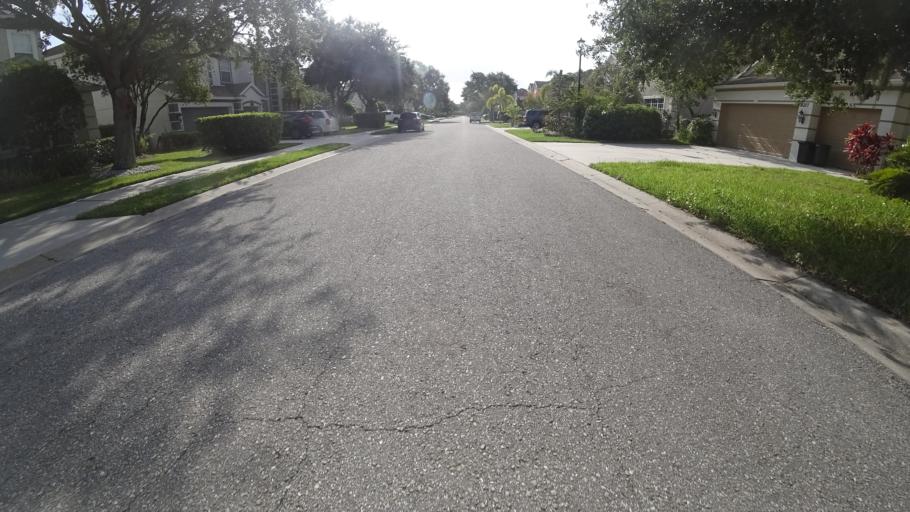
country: US
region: Florida
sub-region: Sarasota County
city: North Sarasota
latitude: 27.4203
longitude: -82.5086
